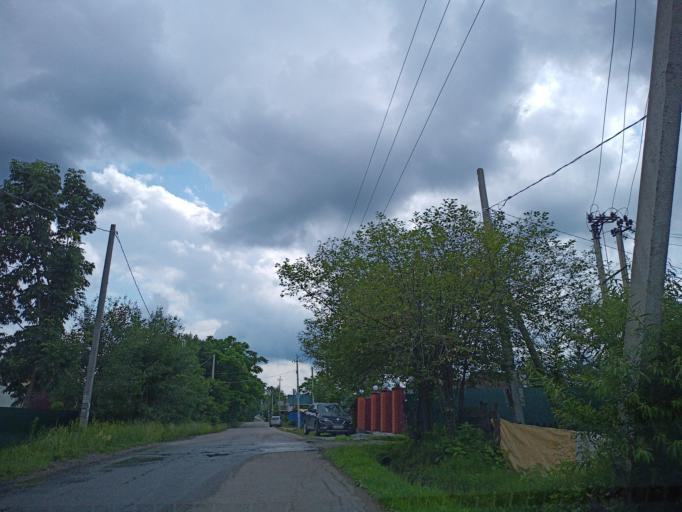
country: RU
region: Khabarovsk Krai
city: Korfovskiy
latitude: 48.3071
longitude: 135.0979
